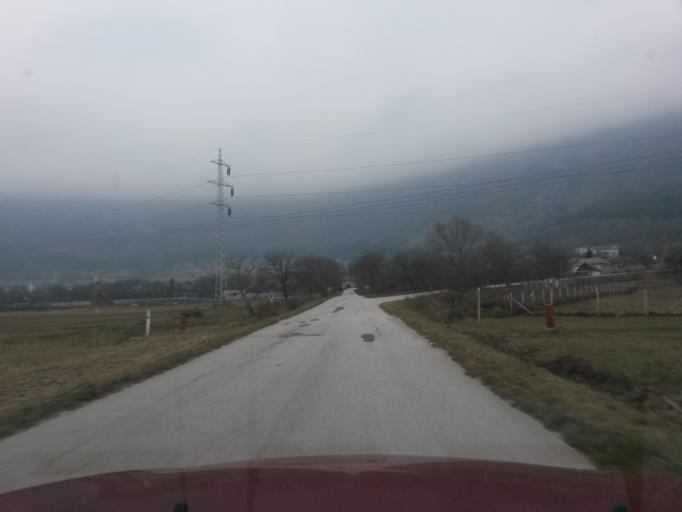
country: SK
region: Kosicky
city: Medzev
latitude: 48.6024
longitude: 20.7581
